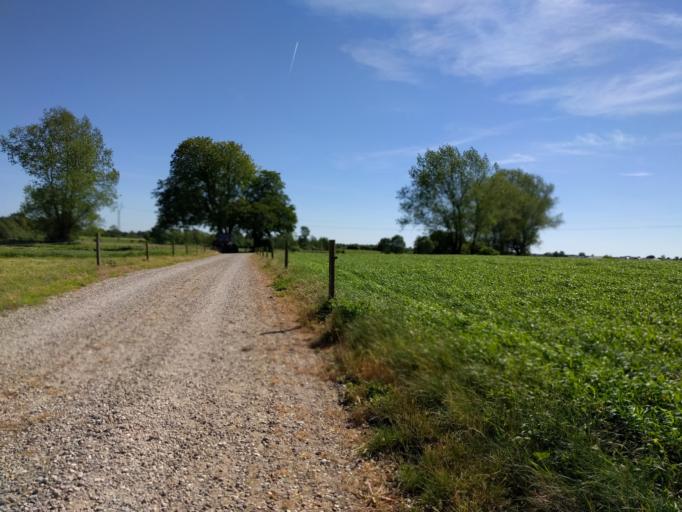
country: DK
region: South Denmark
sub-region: Kerteminde Kommune
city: Langeskov
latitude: 55.3858
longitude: 10.5816
